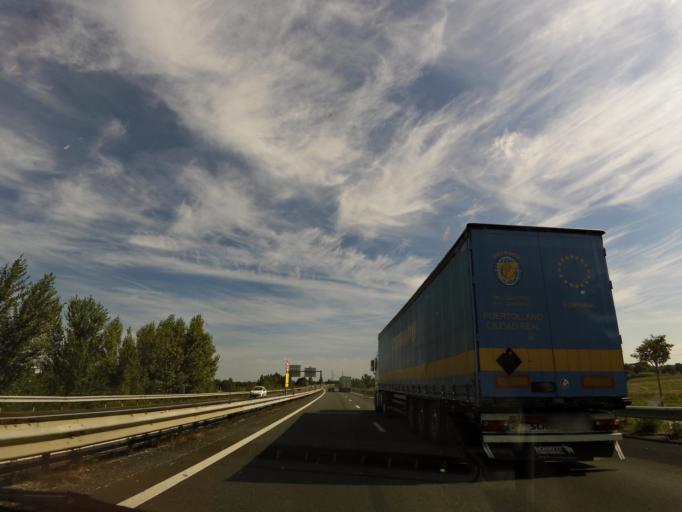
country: FR
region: Languedoc-Roussillon
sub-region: Departement du Gard
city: Caissargues
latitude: 43.8064
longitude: 4.3639
